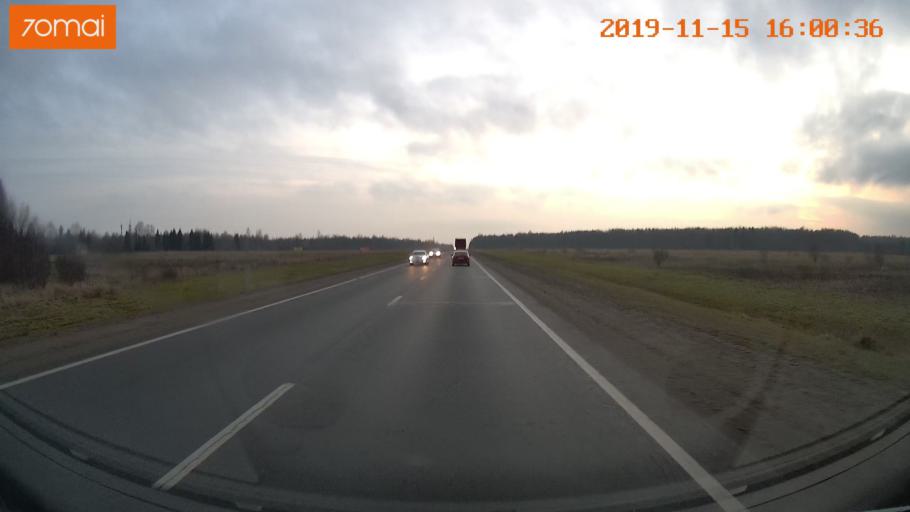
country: RU
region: Jaroslavl
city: Yaroslavl
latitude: 57.7940
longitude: 39.9377
